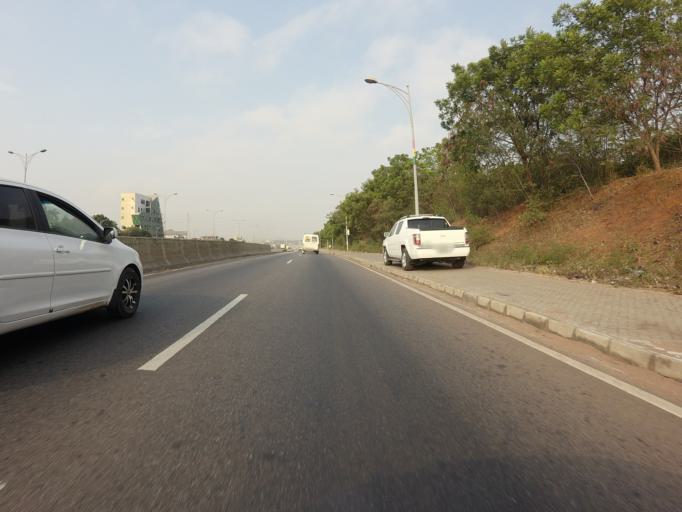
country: GH
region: Greater Accra
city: Dome
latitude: 5.6150
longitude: -0.2173
